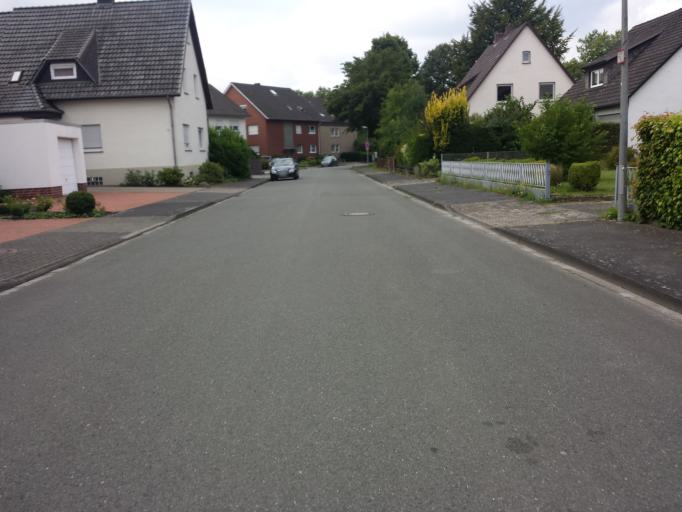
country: DE
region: North Rhine-Westphalia
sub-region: Regierungsbezirk Detmold
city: Guetersloh
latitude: 51.8862
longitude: 8.3849
